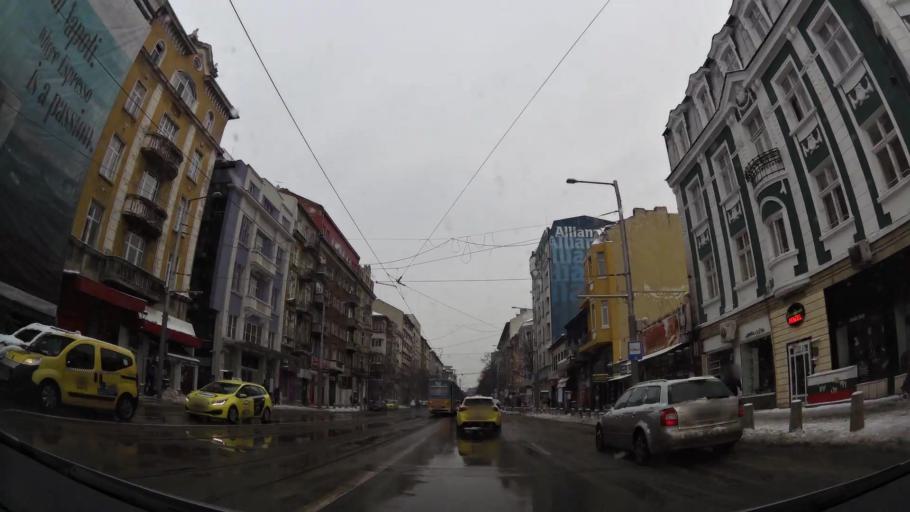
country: BG
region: Sofia-Capital
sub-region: Stolichna Obshtina
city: Sofia
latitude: 42.7045
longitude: 23.3237
